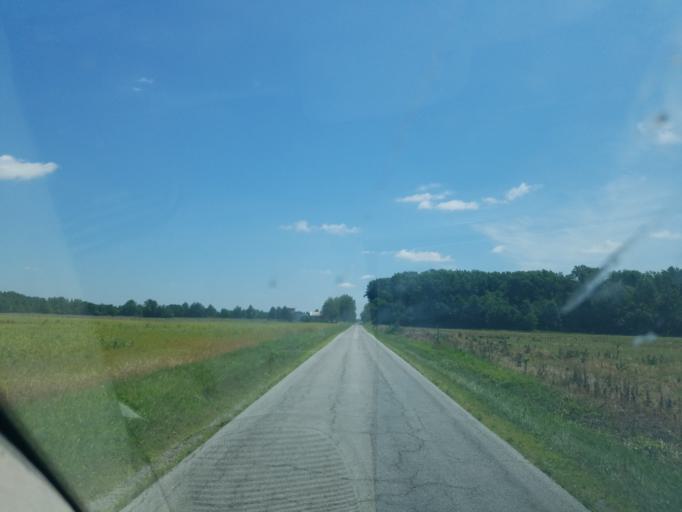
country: US
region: Ohio
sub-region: Hancock County
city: Arlington
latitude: 40.8484
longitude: -83.6306
